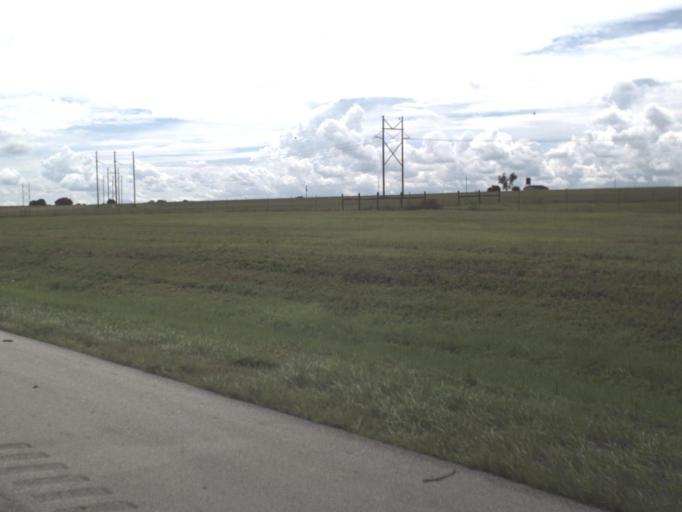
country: US
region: Florida
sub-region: Polk County
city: Polk City
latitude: 28.1574
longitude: -81.8186
